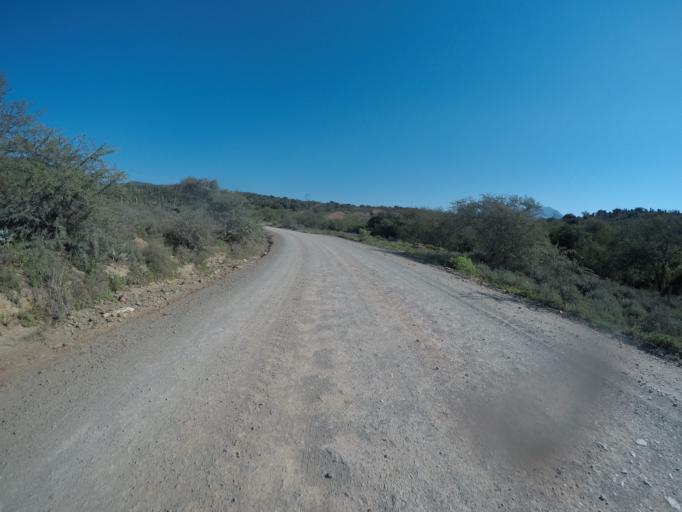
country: ZA
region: Eastern Cape
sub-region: Cacadu District Municipality
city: Kruisfontein
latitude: -33.6744
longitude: 24.5774
